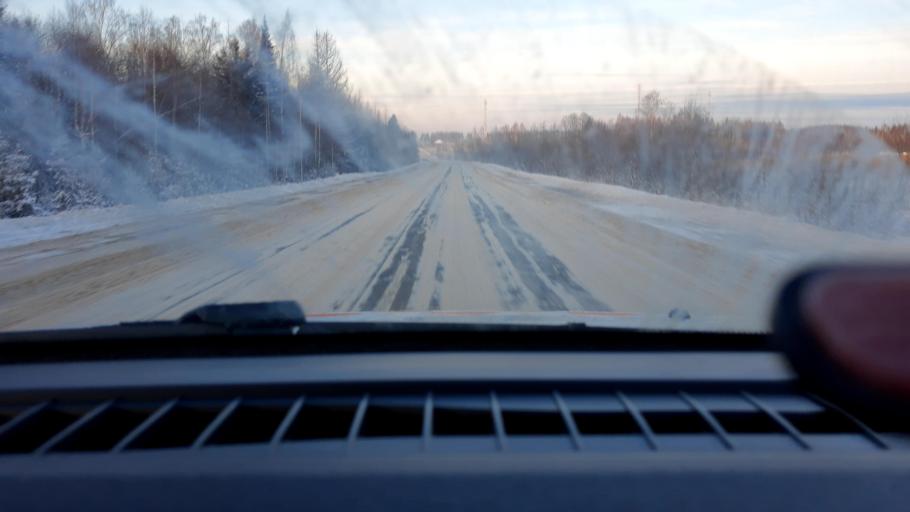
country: RU
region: Nizjnij Novgorod
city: Tonkino
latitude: 57.3628
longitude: 46.4246
